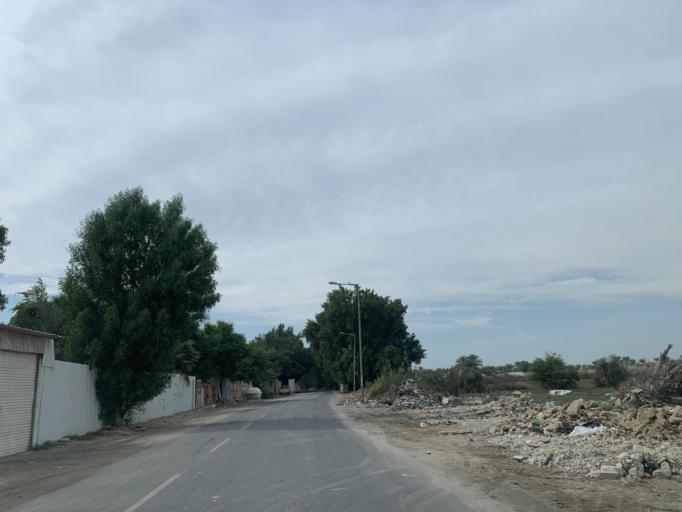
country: BH
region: Central Governorate
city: Madinat Hamad
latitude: 26.1160
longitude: 50.4741
